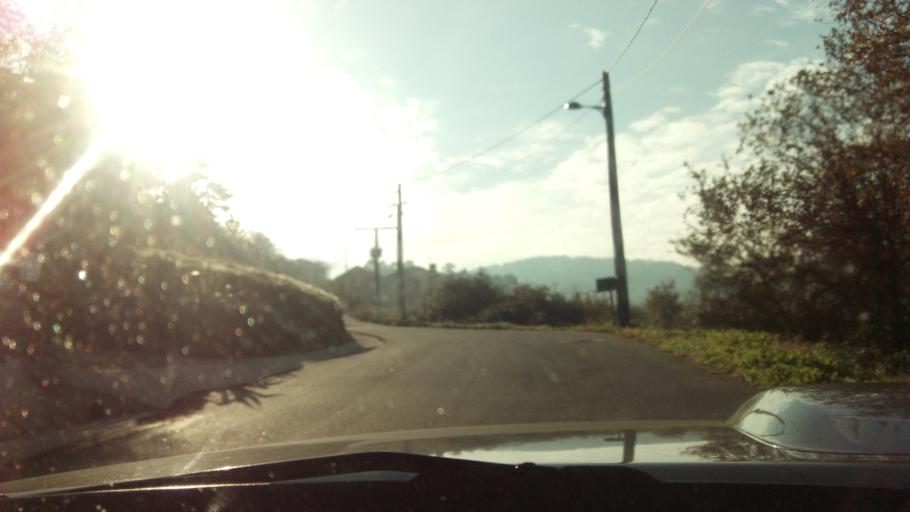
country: ES
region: Galicia
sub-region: Provincia de Pontevedra
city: Marin
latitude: 42.3611
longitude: -8.7341
